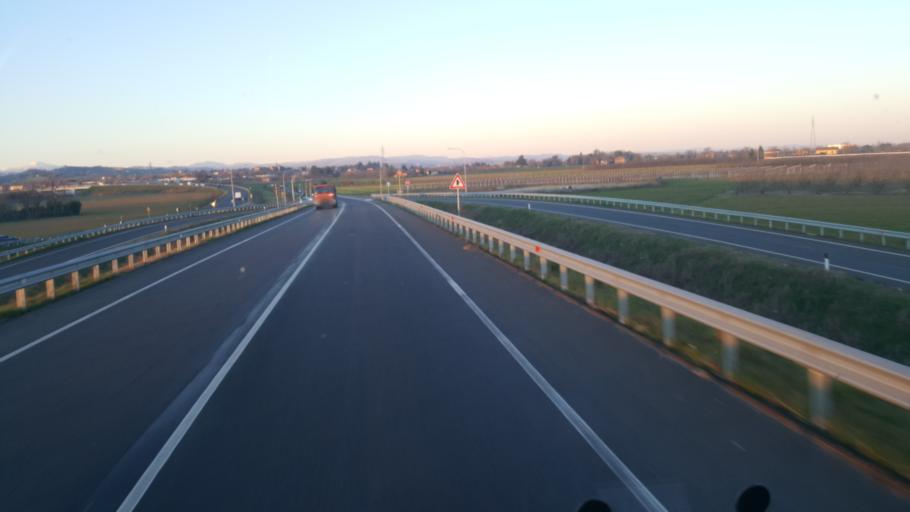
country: IT
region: Emilia-Romagna
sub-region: Provincia di Bologna
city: Crespellano
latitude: 44.5158
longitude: 11.1121
